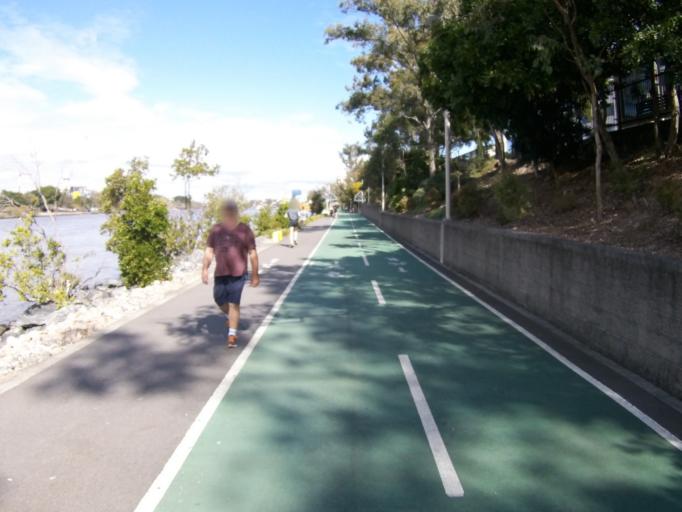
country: AU
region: Queensland
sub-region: Brisbane
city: Milton
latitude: -27.4710
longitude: 153.0082
